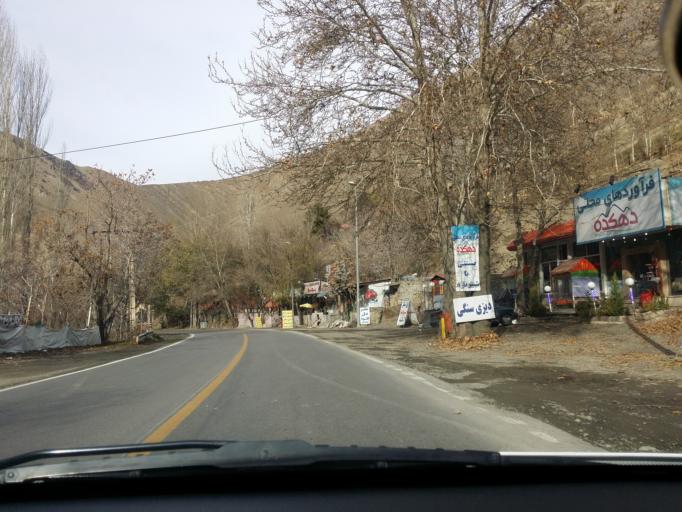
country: IR
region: Alborz
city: Karaj
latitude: 36.0396
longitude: 51.1889
